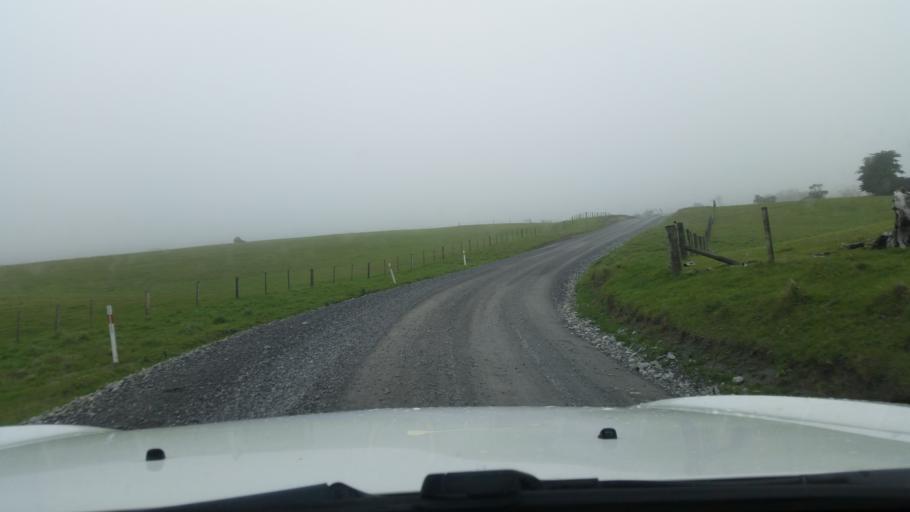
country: NZ
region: Chatham Islands
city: Waitangi
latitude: -43.8155
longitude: -176.5812
